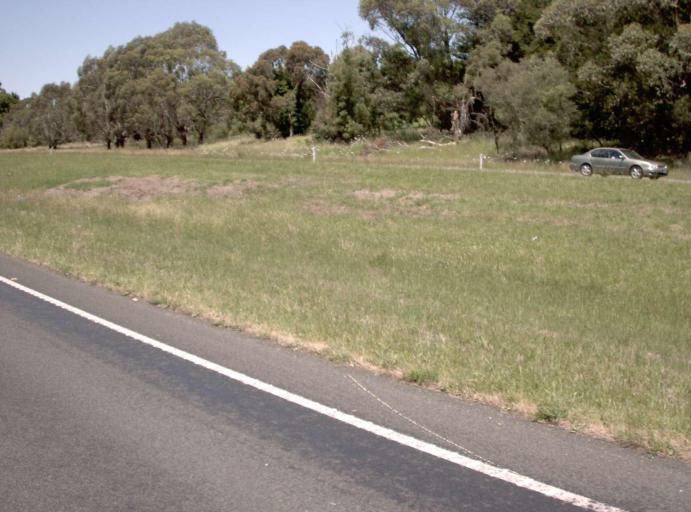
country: AU
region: Victoria
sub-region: Baw Baw
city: Warragul
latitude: -38.1015
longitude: 145.8531
